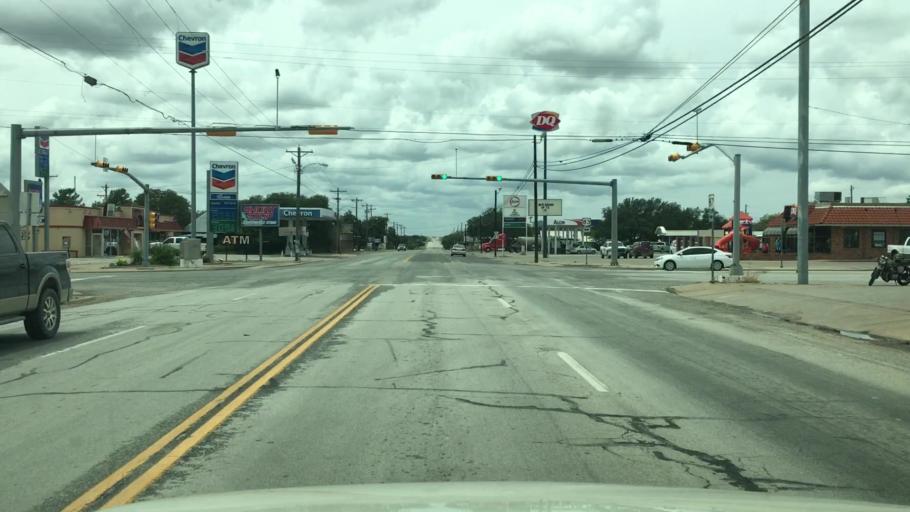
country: US
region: Texas
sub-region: Concho County
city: Eden
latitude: 31.2164
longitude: -99.8453
